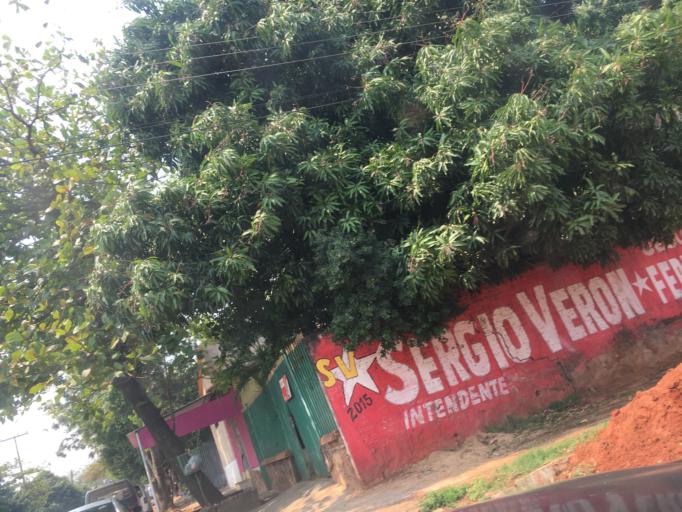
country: PY
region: Central
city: Villa Elisa
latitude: -25.3751
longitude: -57.5933
